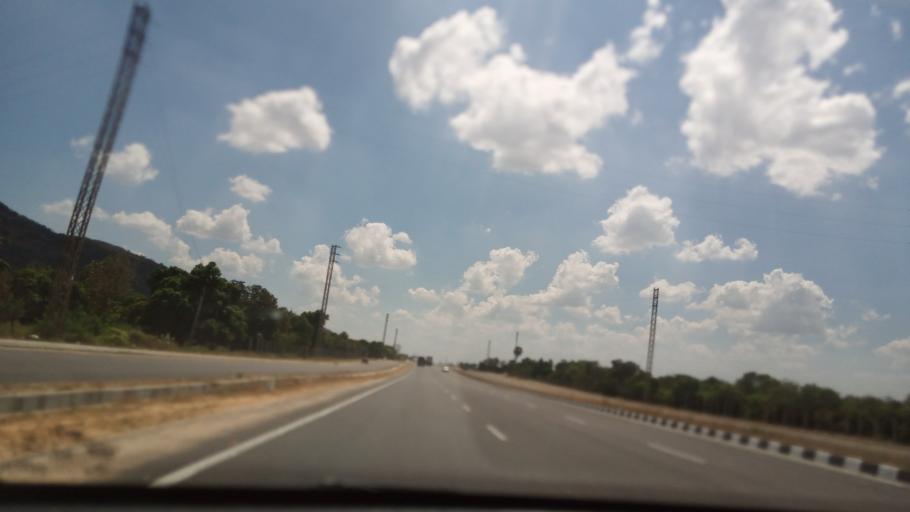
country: IN
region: Andhra Pradesh
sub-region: Chittoor
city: Chittoor
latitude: 13.3262
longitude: 79.0730
